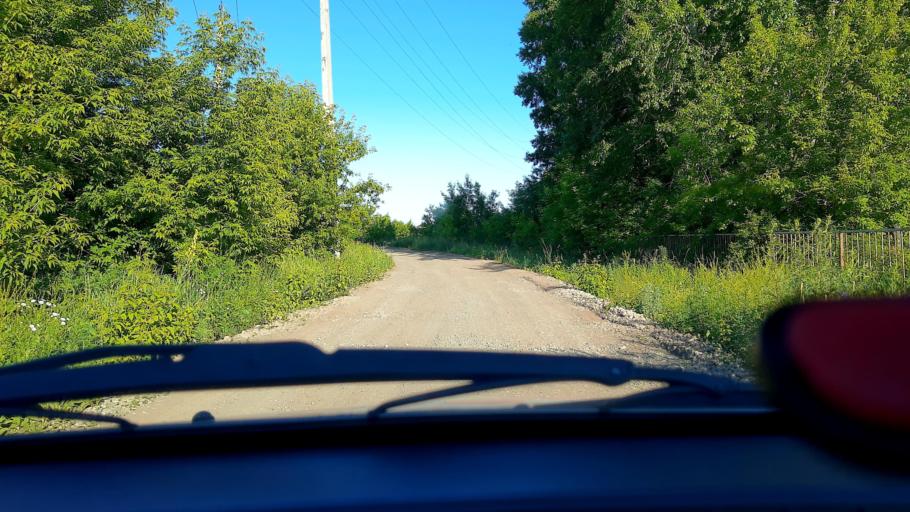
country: RU
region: Bashkortostan
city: Kabakovo
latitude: 54.5144
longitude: 55.9445
